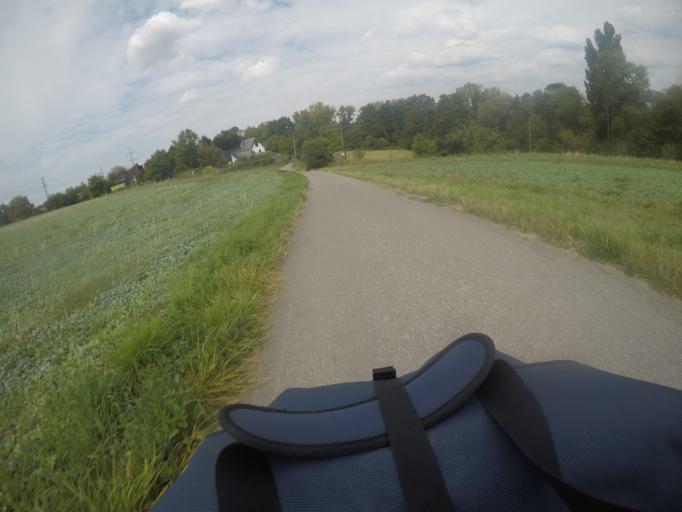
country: DE
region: North Rhine-Westphalia
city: Haan
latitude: 51.2133
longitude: 7.0266
